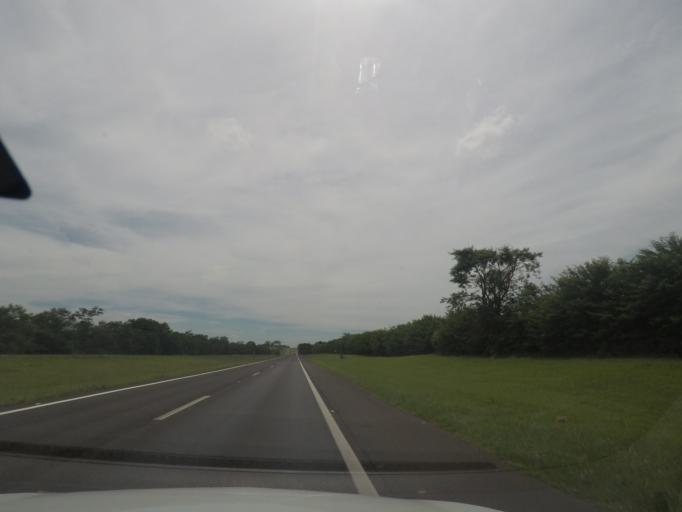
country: BR
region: Sao Paulo
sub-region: Bebedouro
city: Bebedouro
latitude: -20.9778
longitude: -48.4377
